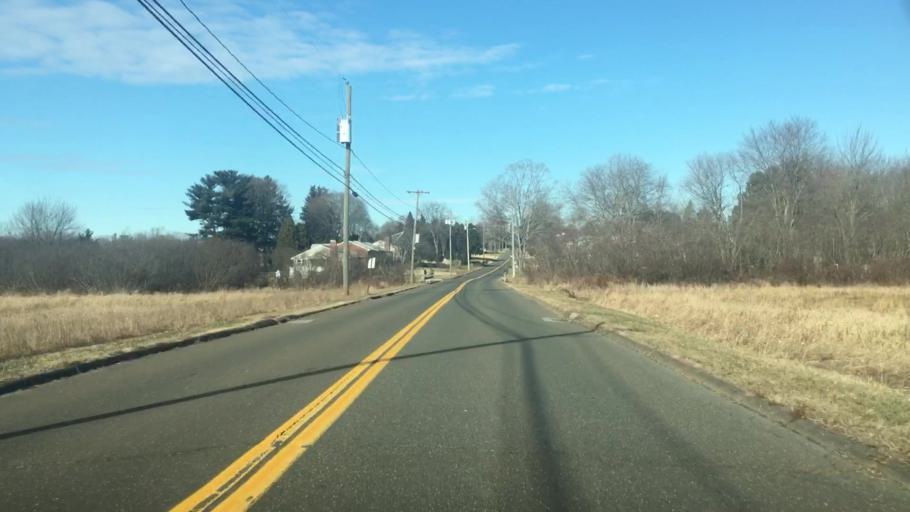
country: US
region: Connecticut
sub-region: Middlesex County
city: Middletown
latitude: 41.5268
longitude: -72.6500
